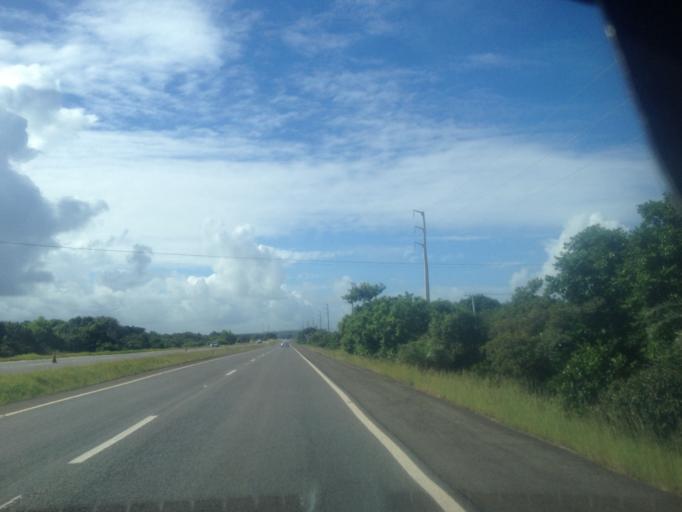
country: BR
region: Bahia
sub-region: Mata De Sao Joao
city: Mata de Sao Joao
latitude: -12.6232
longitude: -38.0601
